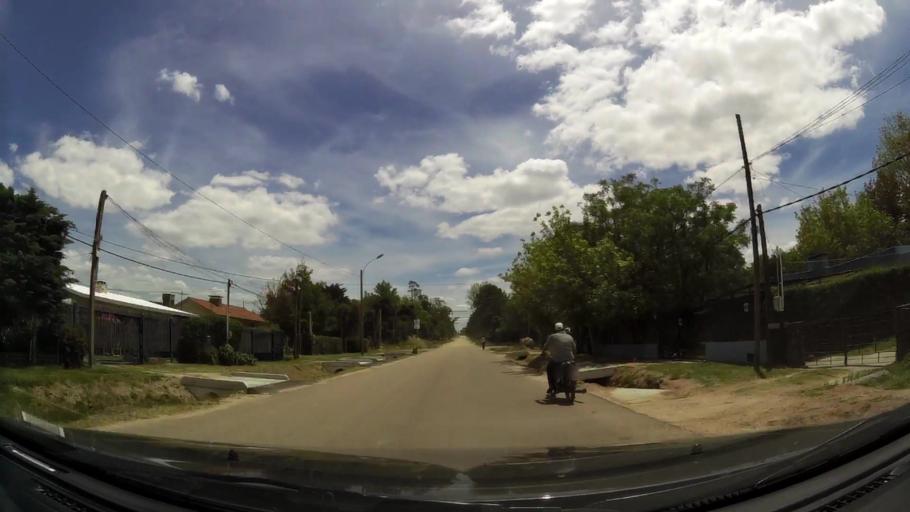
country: UY
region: Canelones
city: Colonia Nicolich
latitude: -34.8219
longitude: -55.9693
